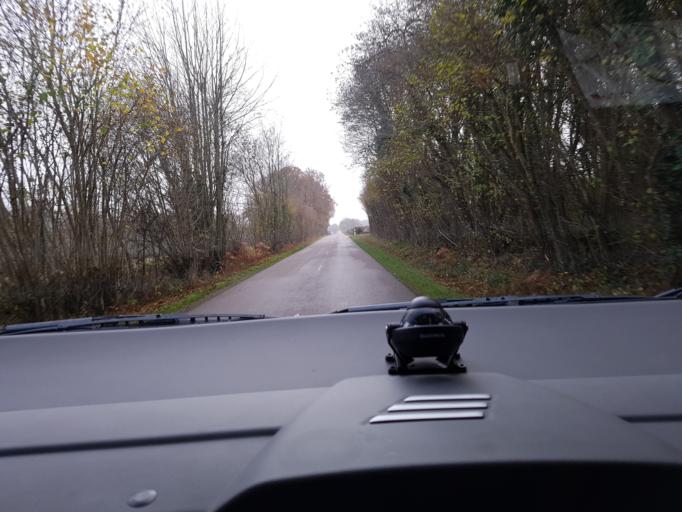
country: FR
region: Lower Normandy
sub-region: Departement de l'Orne
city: Mortree
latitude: 48.6368
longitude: -0.0107
